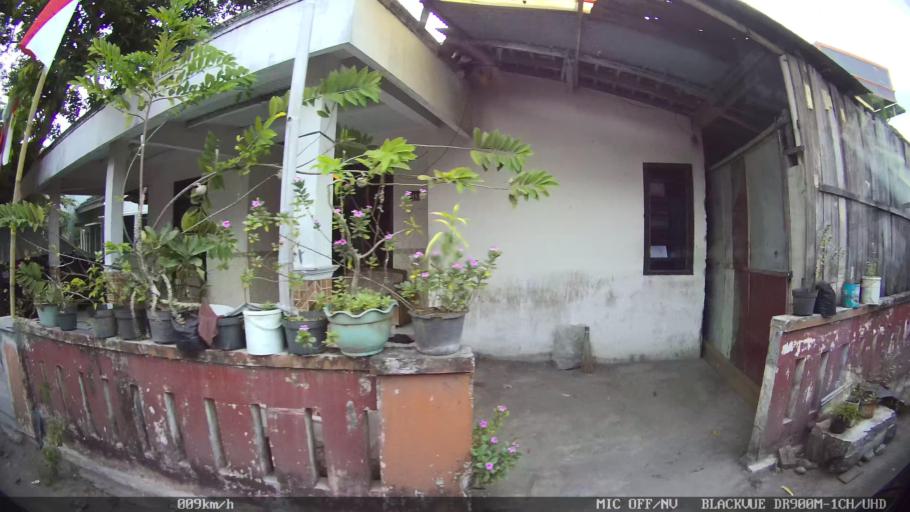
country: ID
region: Daerah Istimewa Yogyakarta
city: Kasihan
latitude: -7.8180
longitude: 110.3267
